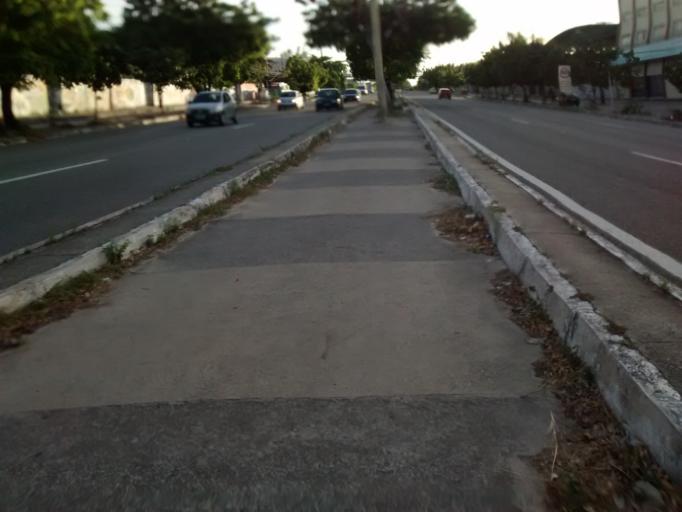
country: BR
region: Ceara
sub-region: Fortaleza
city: Fortaleza
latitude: -3.7375
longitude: -38.5761
